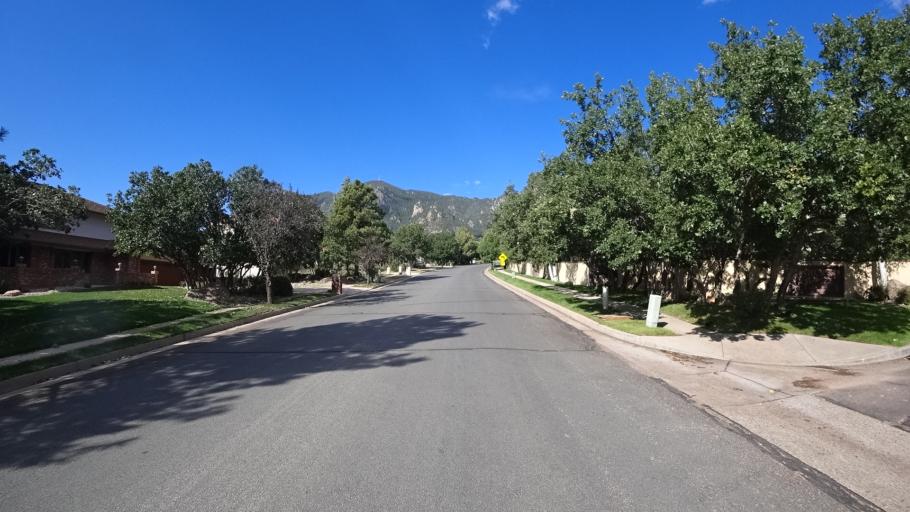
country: US
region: Colorado
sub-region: El Paso County
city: Fort Carson
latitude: 38.7643
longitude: -104.8347
